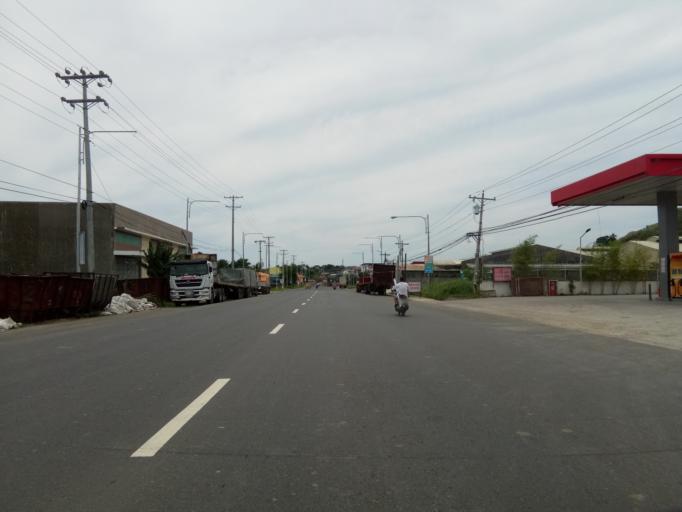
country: PH
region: Caraga
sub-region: Province of Surigao del Norte
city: Rizal
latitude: 9.7691
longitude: 125.4833
